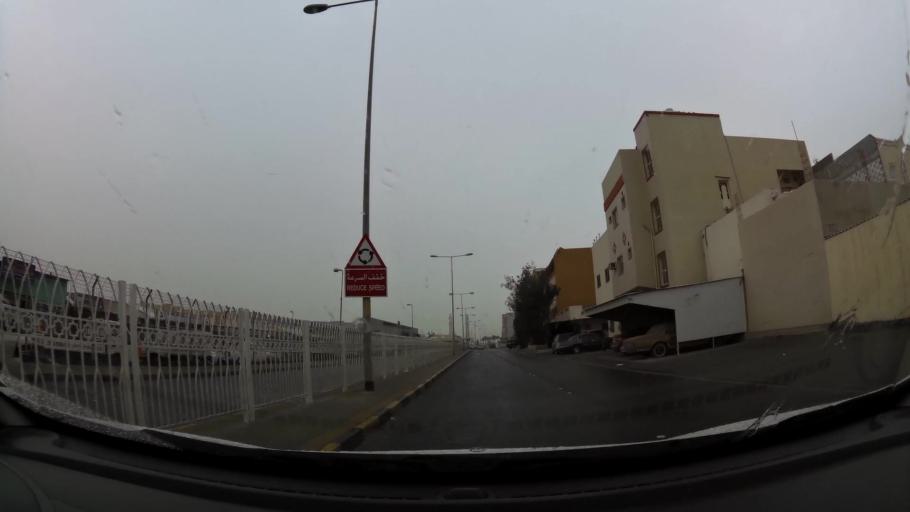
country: BH
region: Northern
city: Madinat `Isa
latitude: 26.1713
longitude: 50.5545
